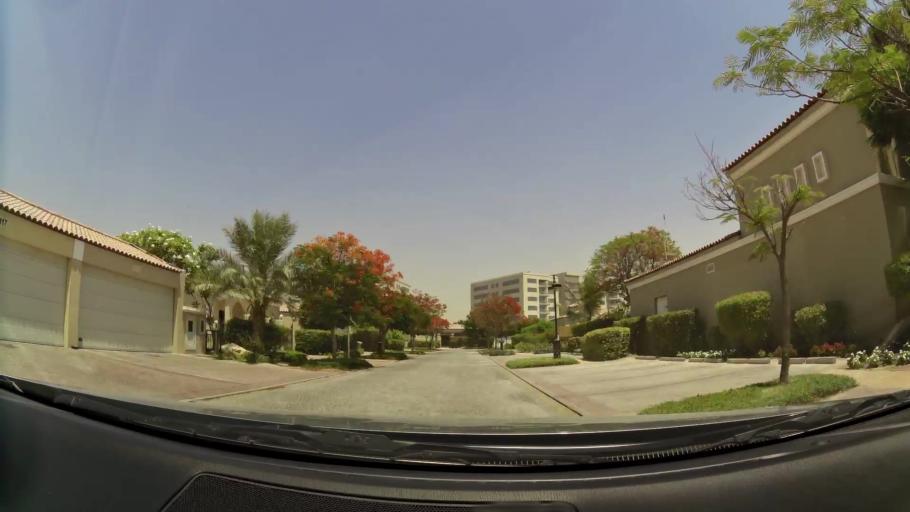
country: AE
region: Dubai
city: Dubai
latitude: 25.0000
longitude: 55.1650
